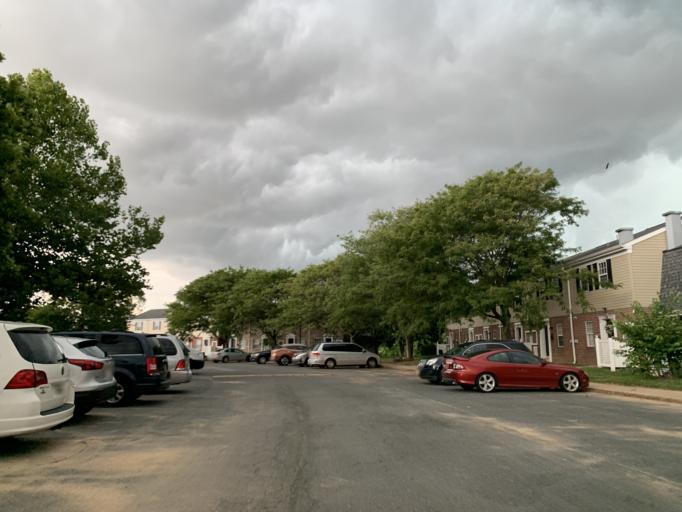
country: US
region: Maryland
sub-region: Baltimore County
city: Essex
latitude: 39.2994
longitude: -76.4551
